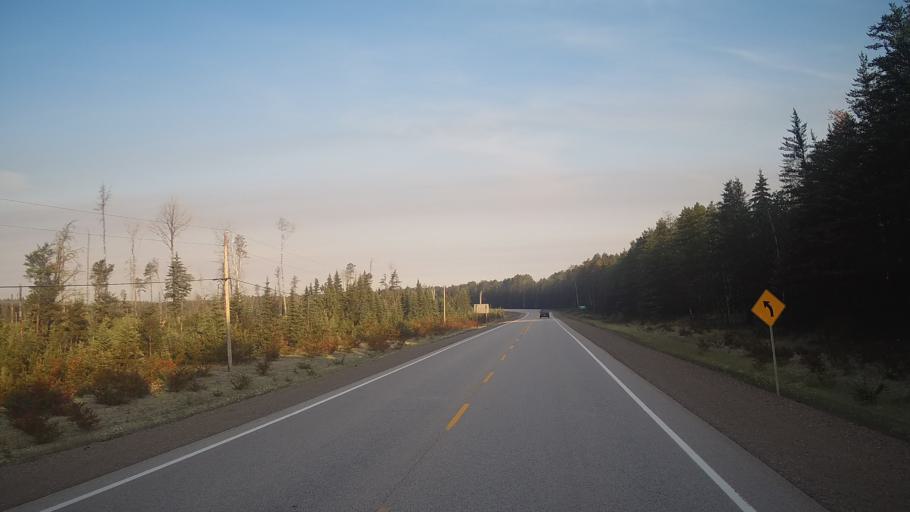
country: CA
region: Ontario
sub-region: Rainy River District
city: Atikokan
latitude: 49.2489
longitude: -91.0556
